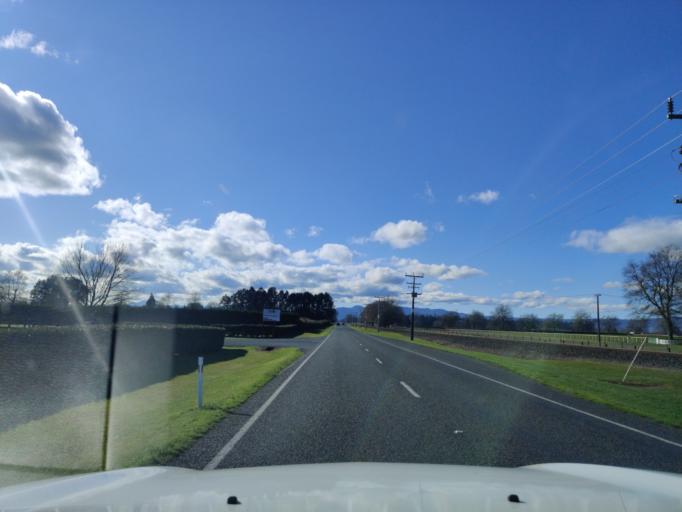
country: NZ
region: Waikato
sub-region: Matamata-Piako District
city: Matamata
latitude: -37.8570
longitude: 175.7565
